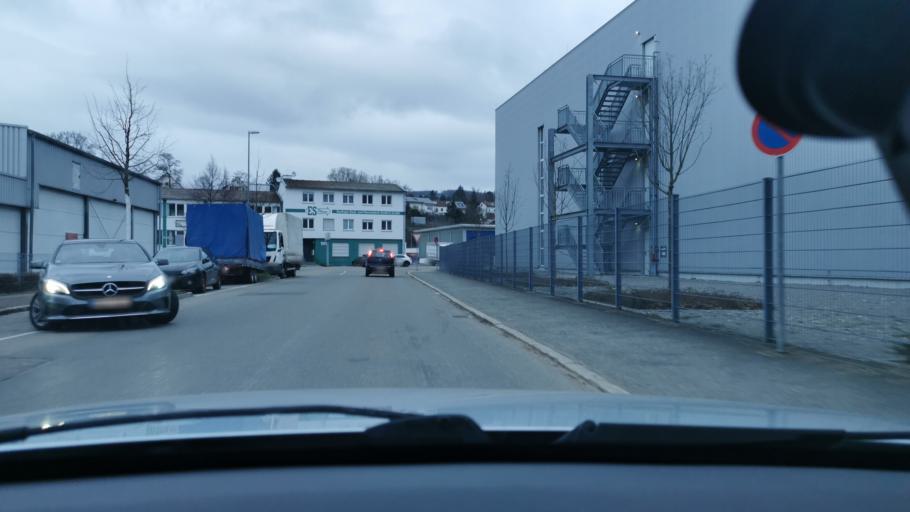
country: DE
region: Baden-Wuerttemberg
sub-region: Regierungsbezirk Stuttgart
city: Denkendorf
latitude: 48.7250
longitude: 9.3408
